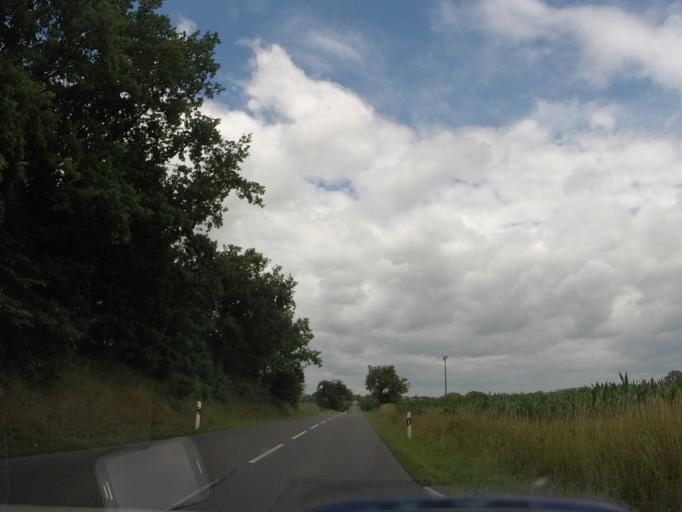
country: DE
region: Mecklenburg-Vorpommern
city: Lalendorf
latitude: 53.7644
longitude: 12.3955
